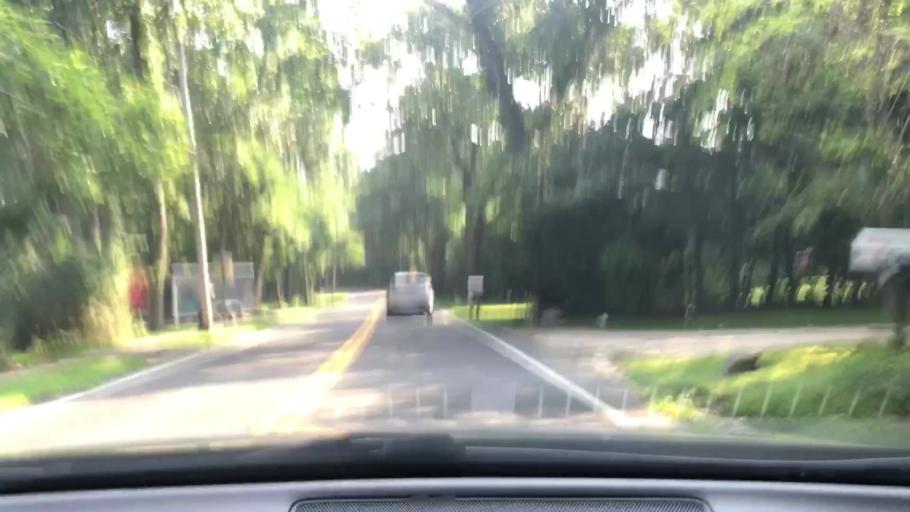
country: US
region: New York
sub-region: Suffolk County
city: Sag Harbor
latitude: 40.9871
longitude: -72.3054
